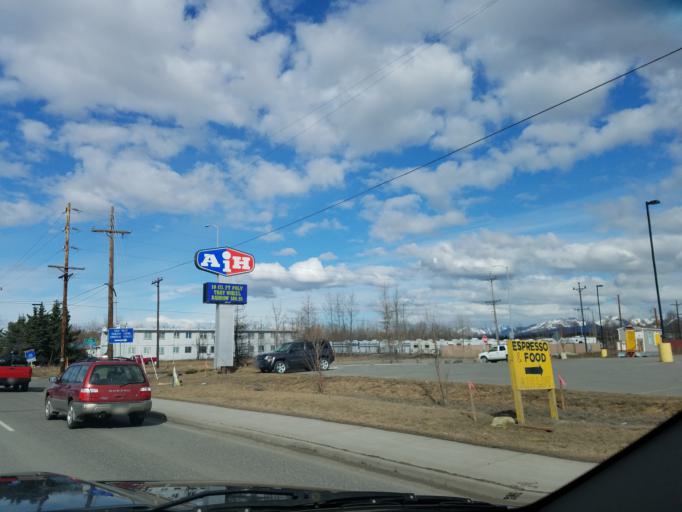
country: US
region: Alaska
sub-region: Anchorage Municipality
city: Anchorage
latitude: 61.1696
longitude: -149.8680
